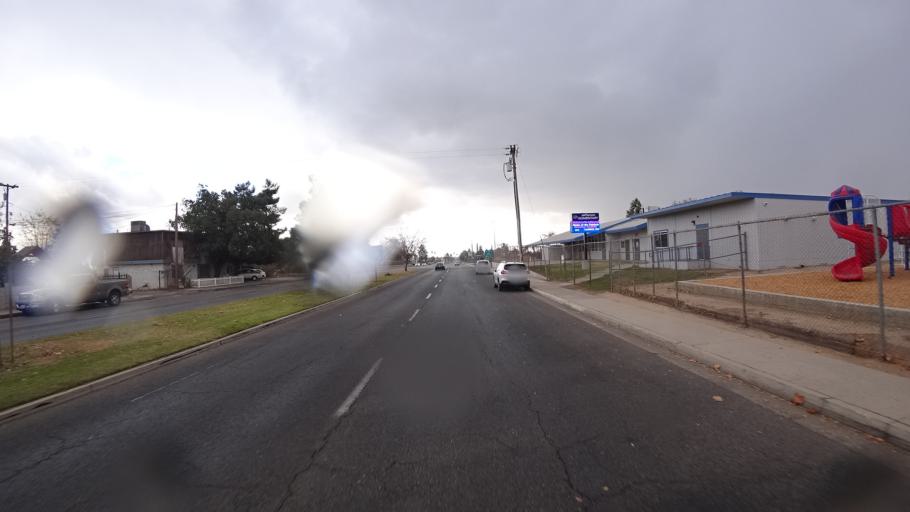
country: US
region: California
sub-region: Kern County
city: Bakersfield
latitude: 35.3873
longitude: -118.9859
